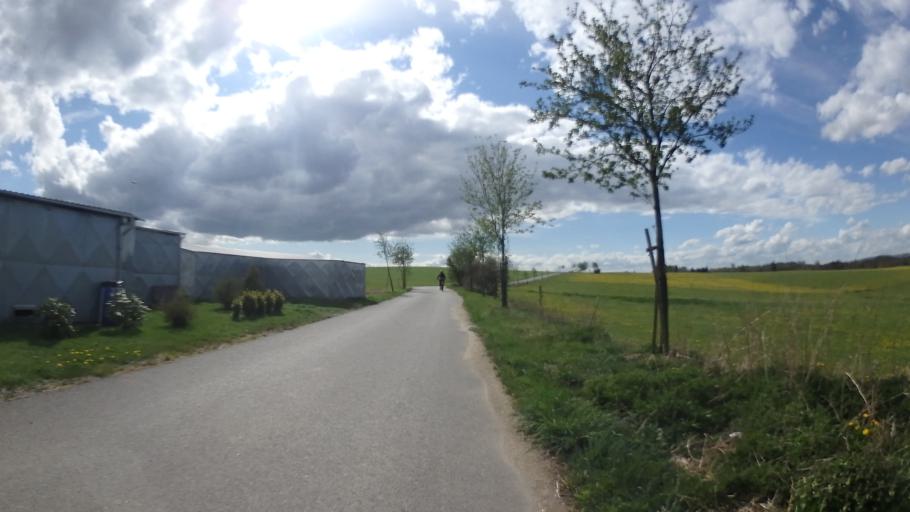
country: CZ
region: Vysocina
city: Merin
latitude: 49.3566
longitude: 15.9264
